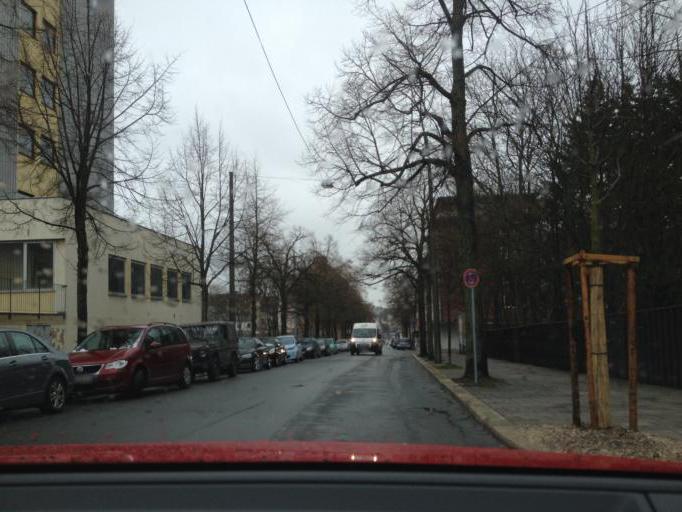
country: DE
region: Bavaria
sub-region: Upper Franconia
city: Hof
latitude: 50.3091
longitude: 11.9230
